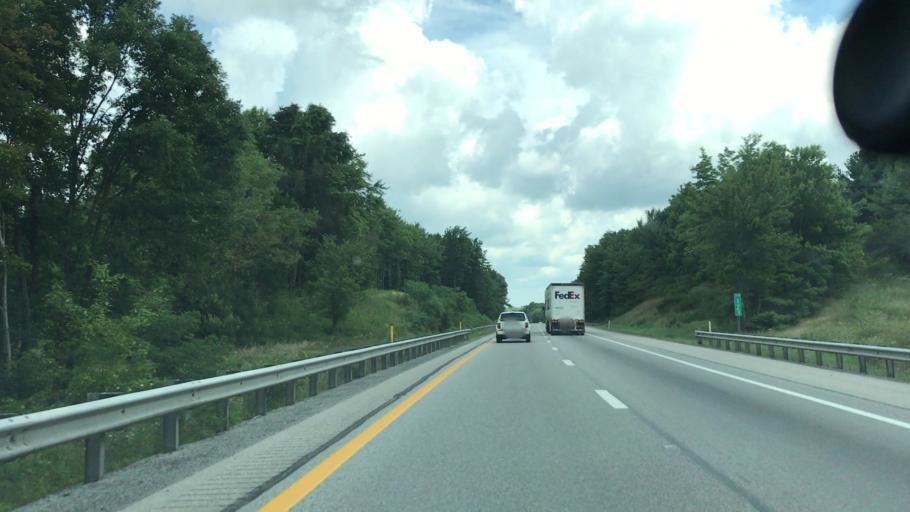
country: US
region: West Virginia
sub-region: Mercer County
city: Athens
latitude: 37.3999
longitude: -81.0622
